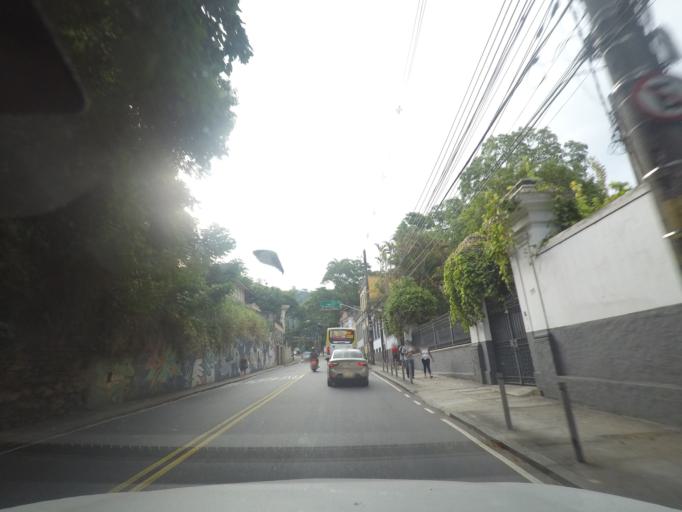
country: BR
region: Rio de Janeiro
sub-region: Rio De Janeiro
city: Rio de Janeiro
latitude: -22.9400
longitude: -43.2007
